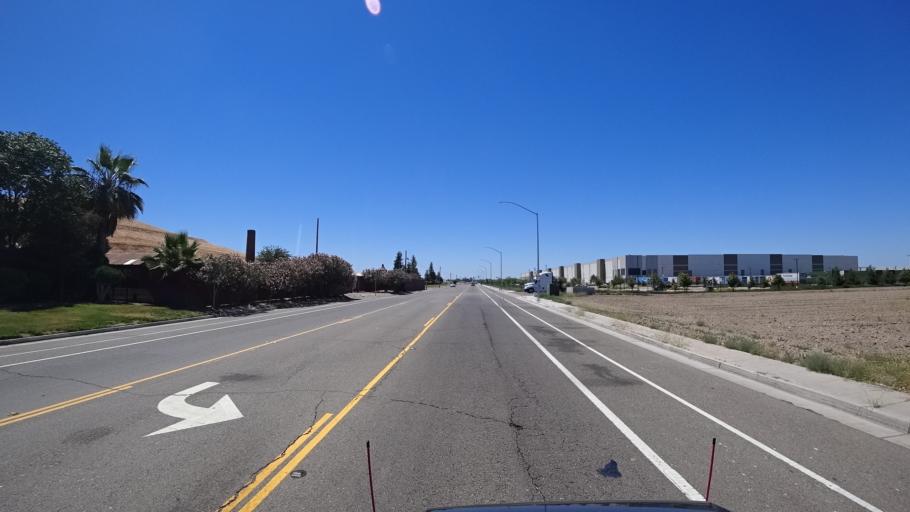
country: US
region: California
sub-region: Fresno County
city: Easton
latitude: 36.6875
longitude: -119.7638
